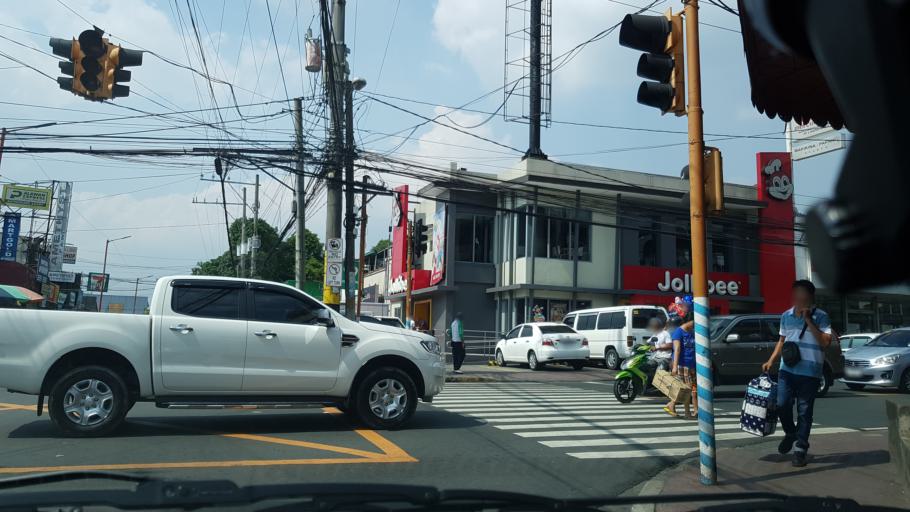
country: PH
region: Calabarzon
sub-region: Province of Rizal
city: Antipolo
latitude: 14.6592
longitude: 121.1134
